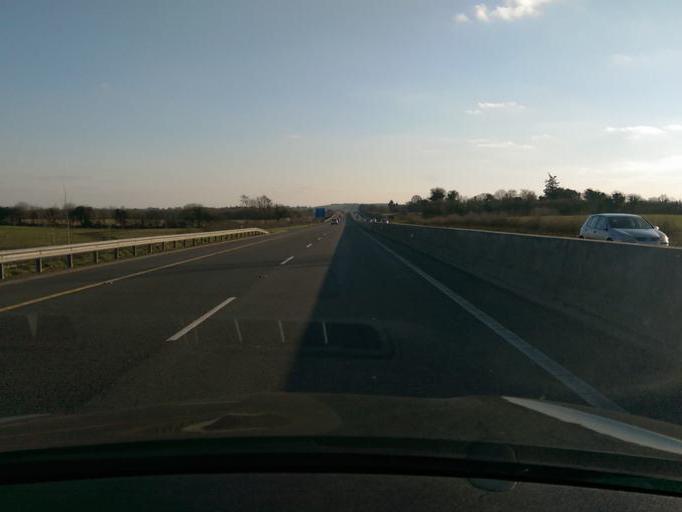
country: IE
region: Leinster
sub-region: Laois
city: Mountrath
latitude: 52.9601
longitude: -7.4405
